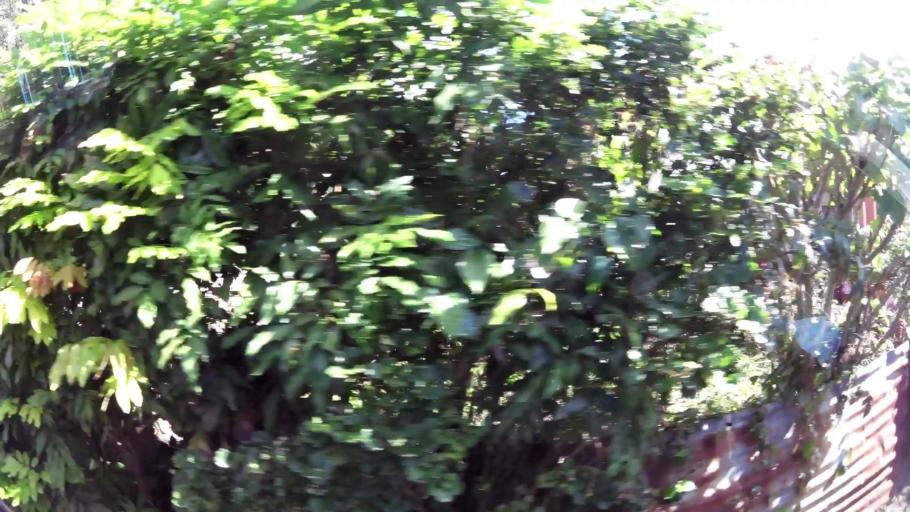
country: MU
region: Grand Port
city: Plaine Magnien
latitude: -20.4276
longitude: 57.6592
